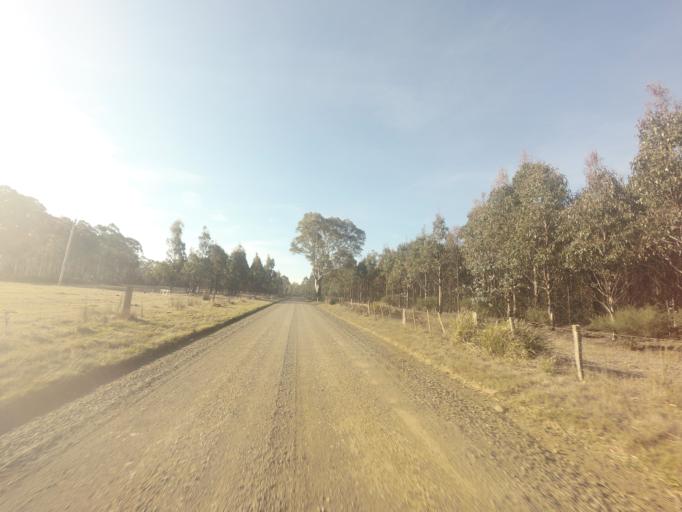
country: AU
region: Tasmania
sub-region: Brighton
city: Bridgewater
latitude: -42.4514
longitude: 147.3839
